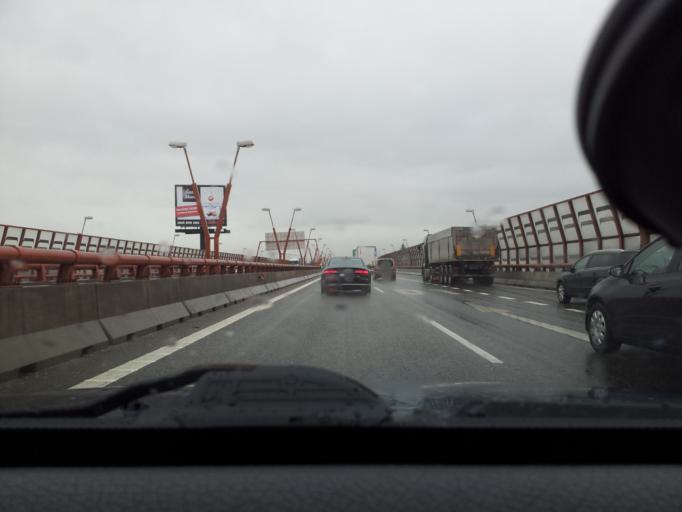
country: SK
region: Bratislavsky
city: Bratislava
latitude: 48.1547
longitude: 17.1815
